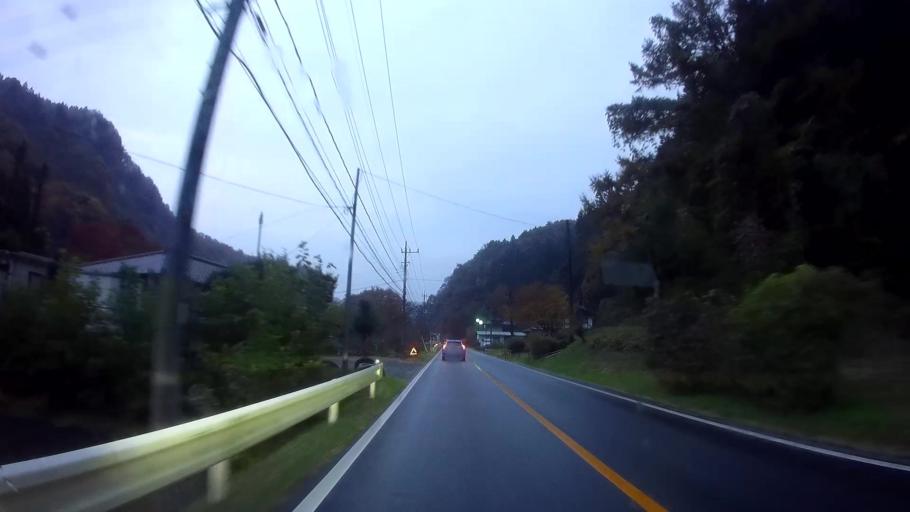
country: JP
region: Gunma
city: Nakanojomachi
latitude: 36.5192
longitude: 138.7796
